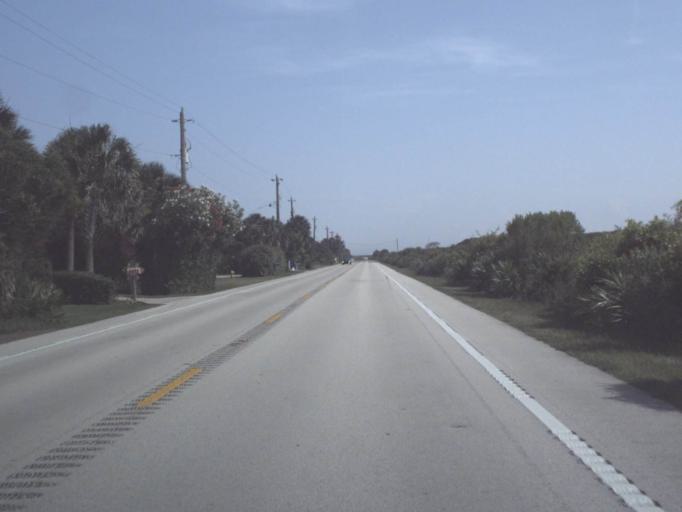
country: US
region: Florida
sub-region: Saint Johns County
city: Villano Beach
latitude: 30.0510
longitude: -81.3304
